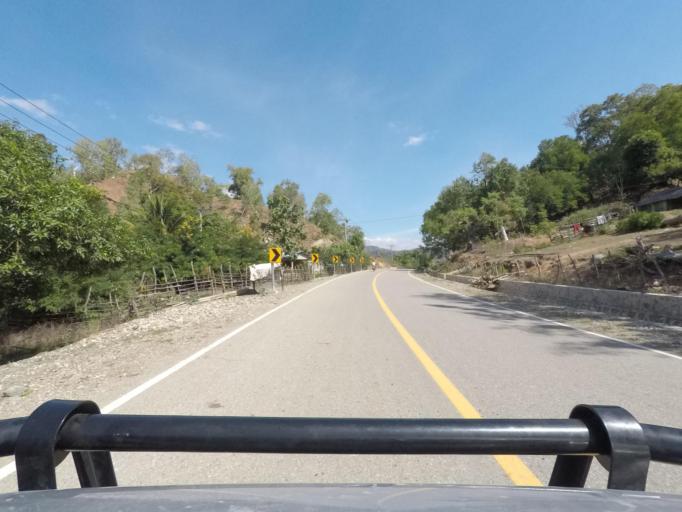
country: TL
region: Bobonaro
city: Maliana
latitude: -8.8734
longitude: 125.0419
